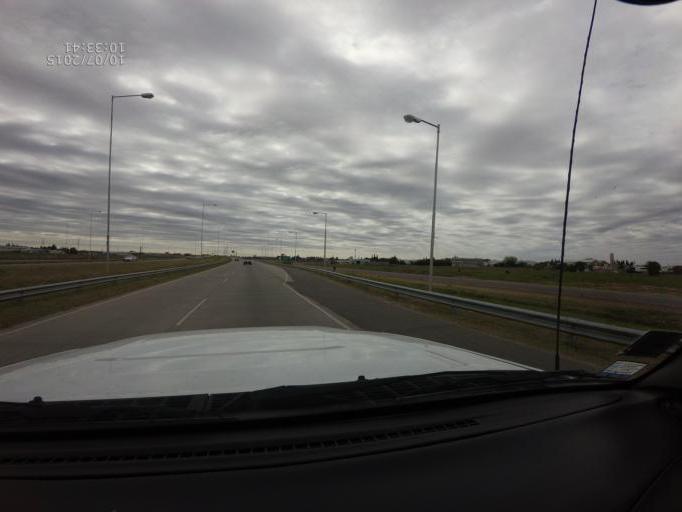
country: AR
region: Cordoba
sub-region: Departamento de Capital
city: Cordoba
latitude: -31.3550
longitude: -64.2085
